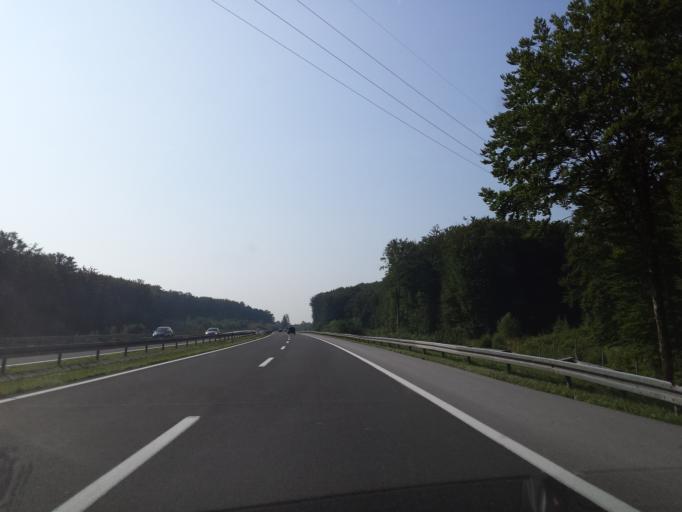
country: HR
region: Karlovacka
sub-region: Grad Ogulin
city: Ogulin
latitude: 45.3642
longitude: 15.2721
